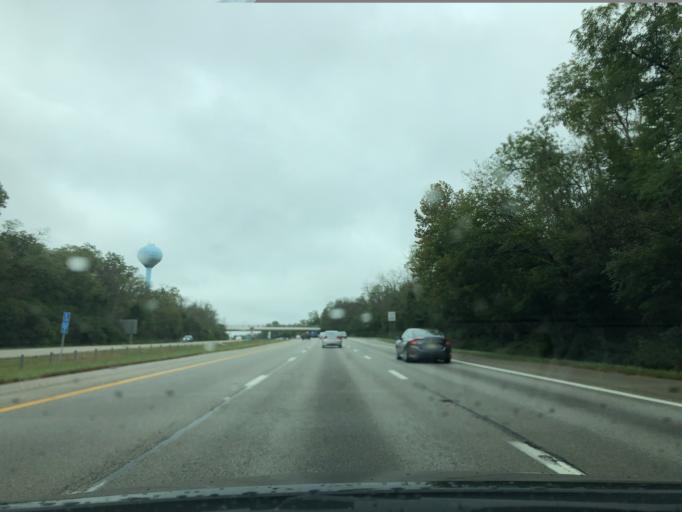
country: US
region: Ohio
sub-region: Hamilton County
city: The Village of Indian Hill
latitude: 39.2364
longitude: -84.2952
